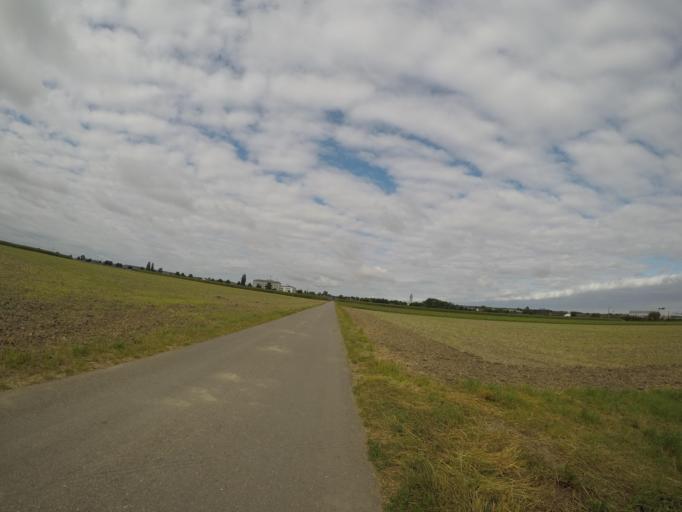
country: DE
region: Baden-Wuerttemberg
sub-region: Tuebingen Region
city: Langenau
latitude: 48.4956
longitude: 10.1373
